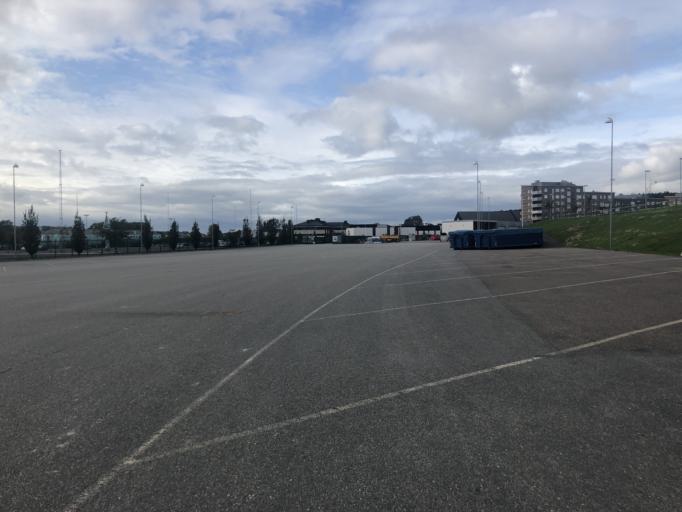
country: SE
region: Vaestra Goetaland
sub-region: Molndal
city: Moelndal
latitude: 57.6488
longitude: 11.9989
